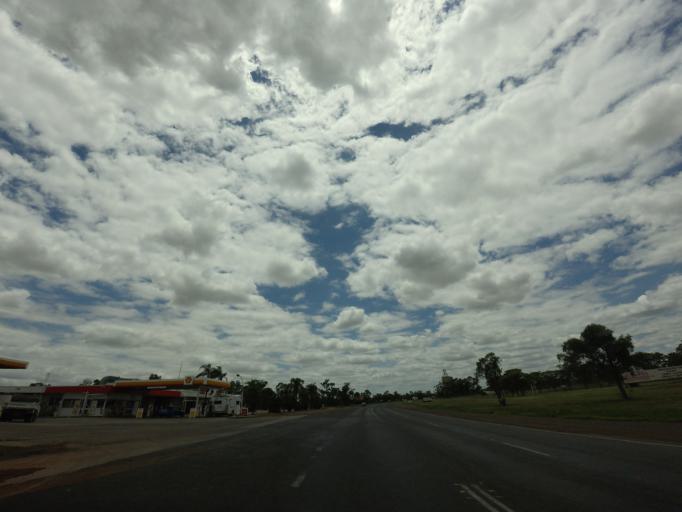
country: AU
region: New South Wales
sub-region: Moree Plains
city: Boggabilla
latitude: -28.6092
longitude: 150.3511
